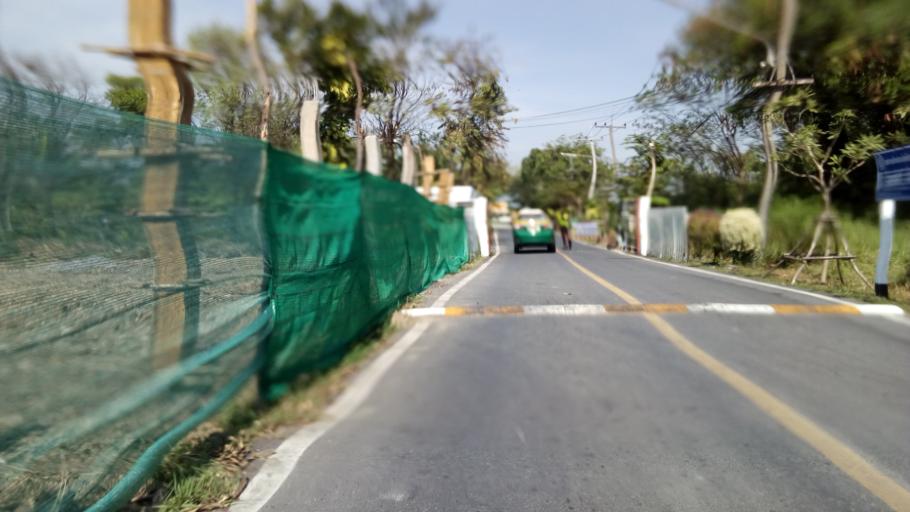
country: TH
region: Pathum Thani
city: Nong Suea
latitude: 14.0650
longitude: 100.8376
